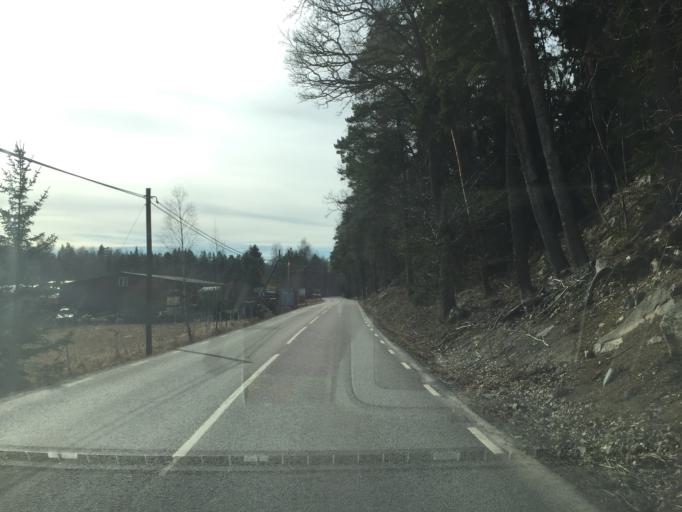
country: SE
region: Stockholm
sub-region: Botkyrka Kommun
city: Tullinge
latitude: 59.1092
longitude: 17.9896
